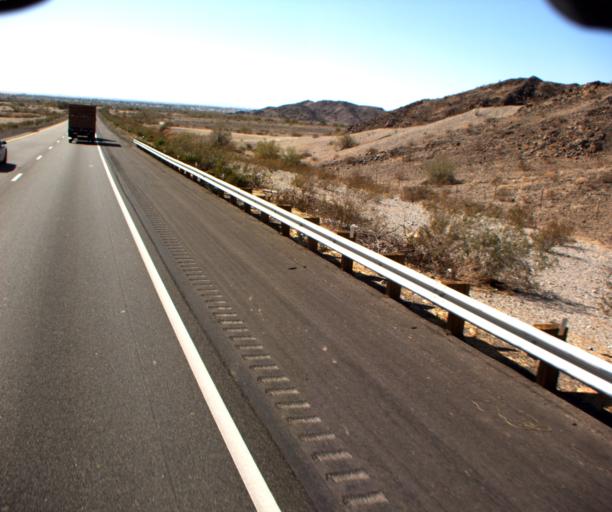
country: US
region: Arizona
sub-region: Yuma County
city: Fortuna Foothills
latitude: 32.6608
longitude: -114.3588
